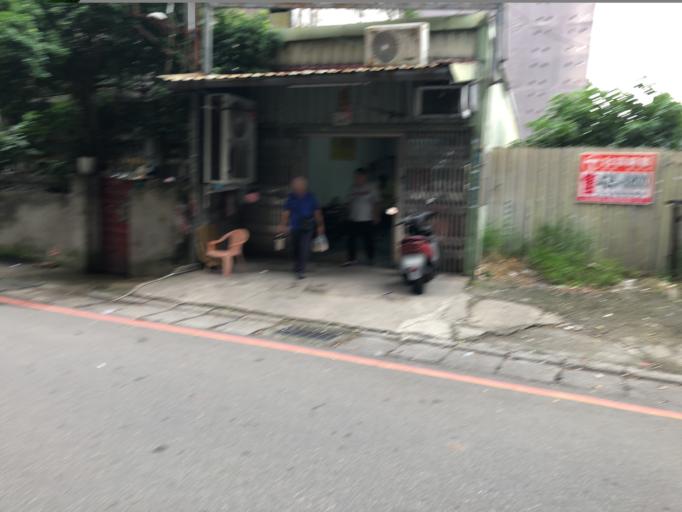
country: TW
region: Taiwan
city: Taoyuan City
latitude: 24.9654
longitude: 121.2518
